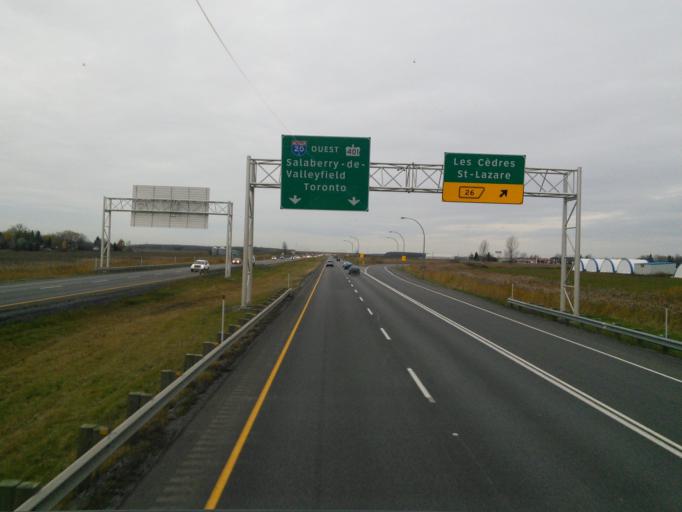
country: CA
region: Quebec
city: Les Cedres
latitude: 45.3448
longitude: -74.0778
